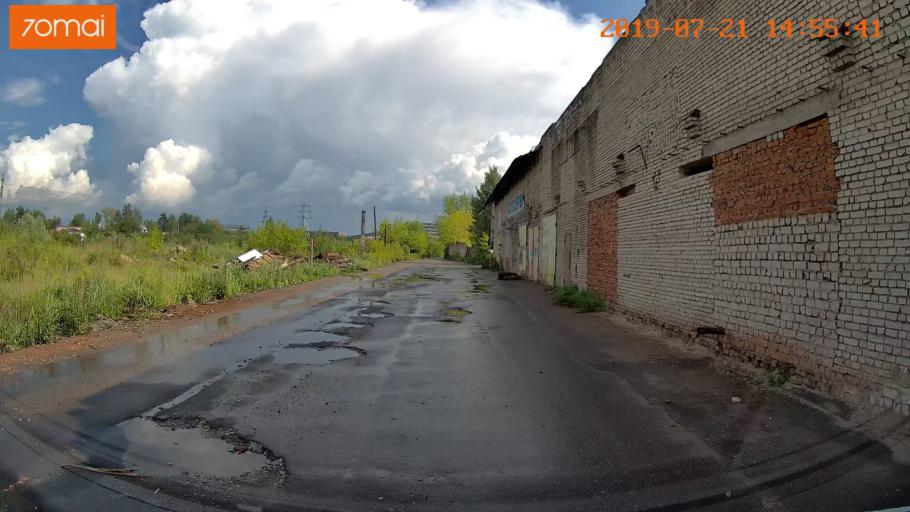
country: RU
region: Ivanovo
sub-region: Gorod Ivanovo
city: Ivanovo
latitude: 56.9653
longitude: 41.0306
